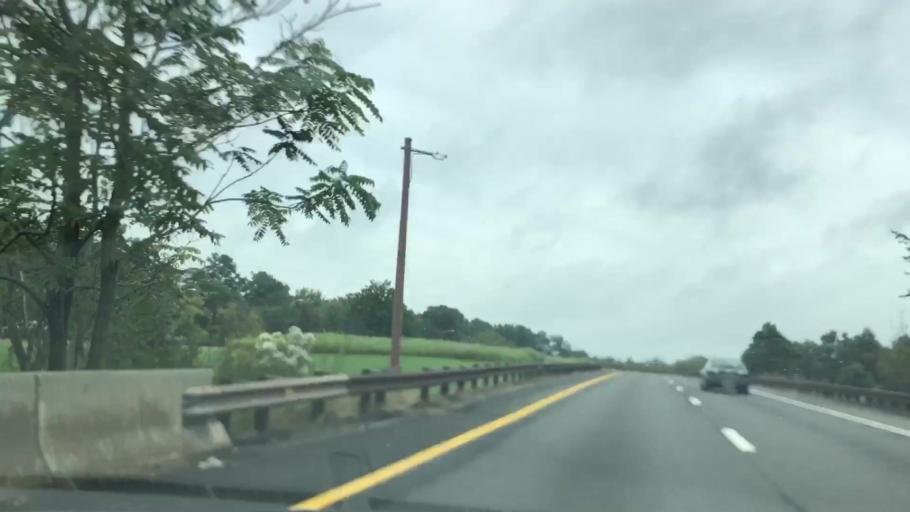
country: US
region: New York
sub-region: Rockland County
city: Chestnut Ridge
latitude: 41.0555
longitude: -74.0654
